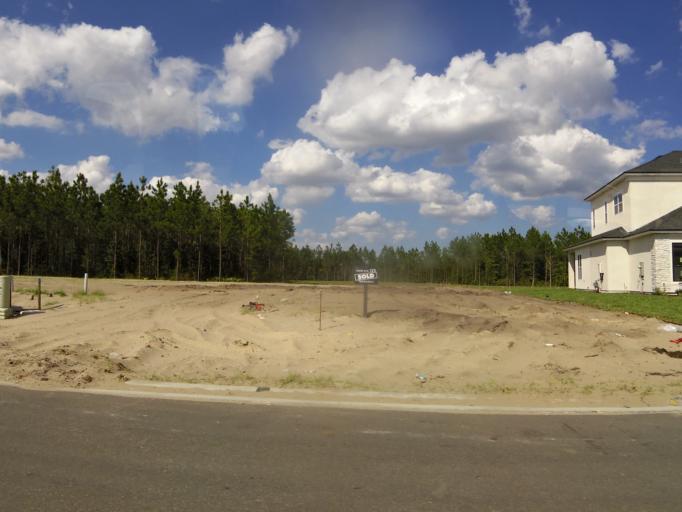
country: US
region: Florida
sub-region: Saint Johns County
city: Palm Valley
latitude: 30.1967
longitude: -81.5053
